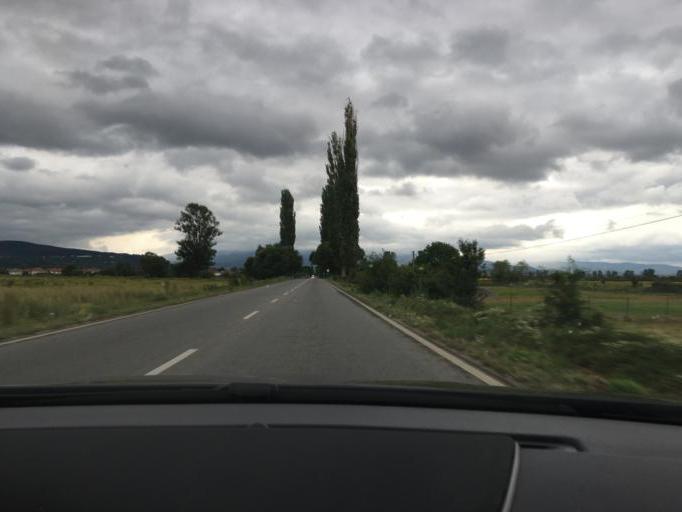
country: BG
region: Kyustendil
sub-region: Obshtina Kyustendil
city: Kyustendil
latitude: 42.2767
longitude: 22.7473
